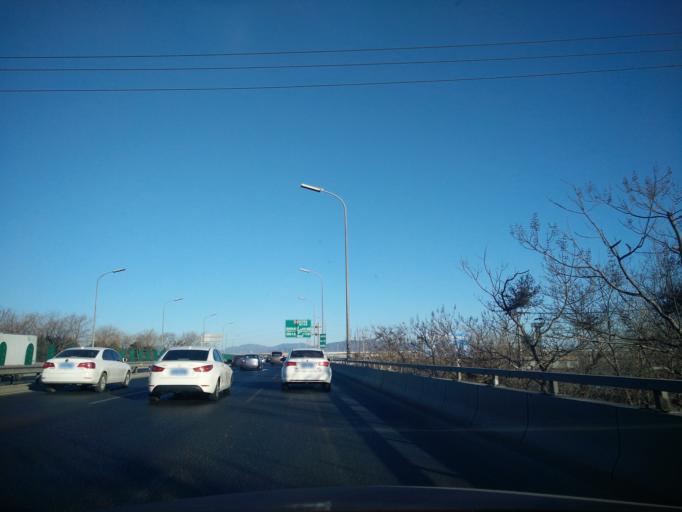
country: CN
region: Beijing
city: Lugu
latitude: 39.8585
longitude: 116.2126
